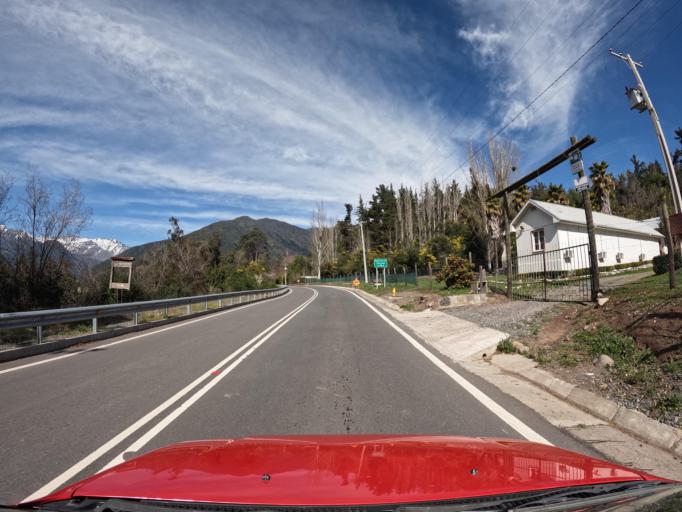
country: CL
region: O'Higgins
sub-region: Provincia de Colchagua
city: Chimbarongo
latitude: -34.9995
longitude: -70.8163
